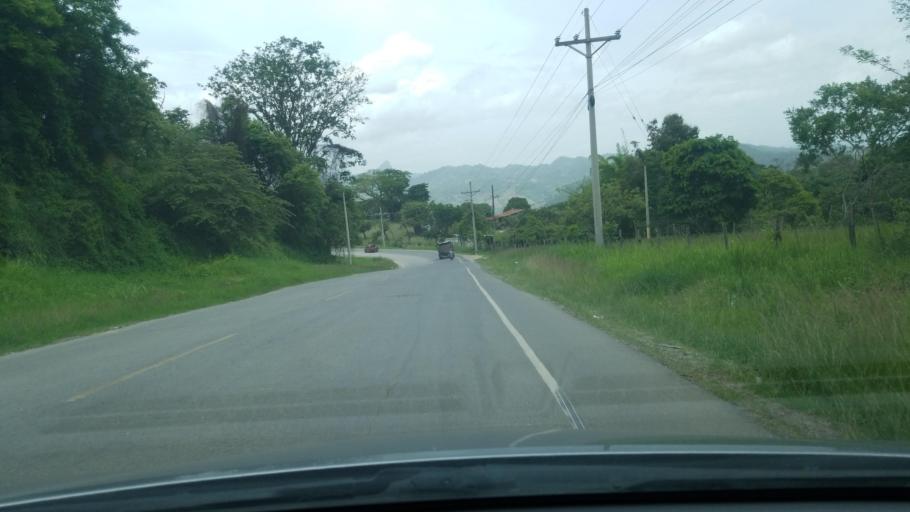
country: HN
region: Copan
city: Santa Rosa de Copan
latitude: 14.7396
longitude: -88.7747
